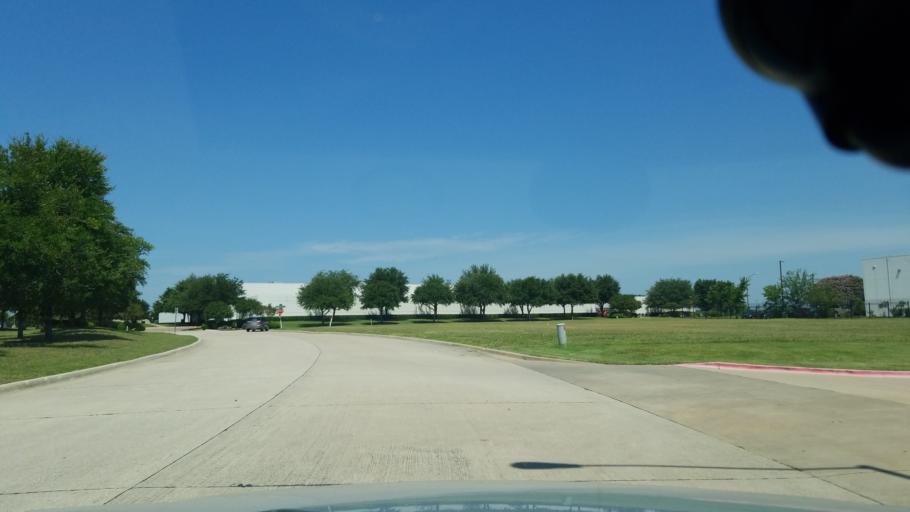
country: US
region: Texas
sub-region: Tarrant County
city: Euless
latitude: 32.8338
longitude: -97.0406
